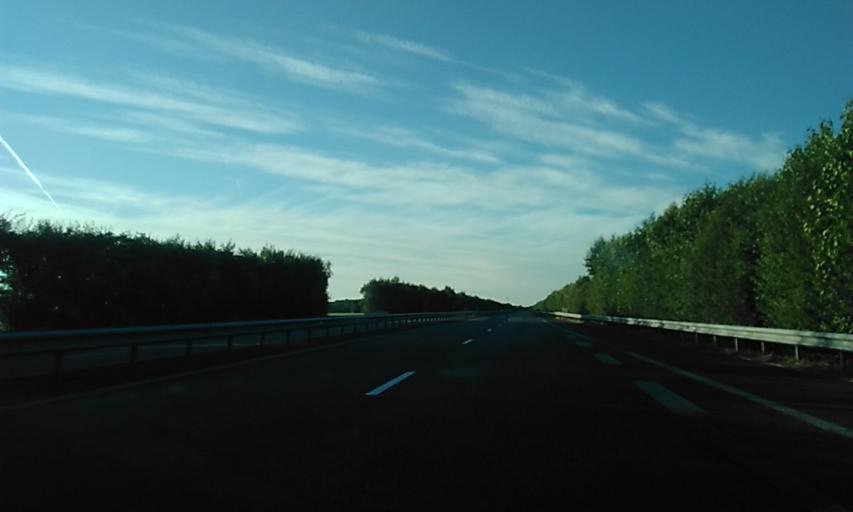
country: FR
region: Brittany
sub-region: Departement d'Ille-et-Vilaine
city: Plelan-le-Grand
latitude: 47.9772
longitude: -2.0980
